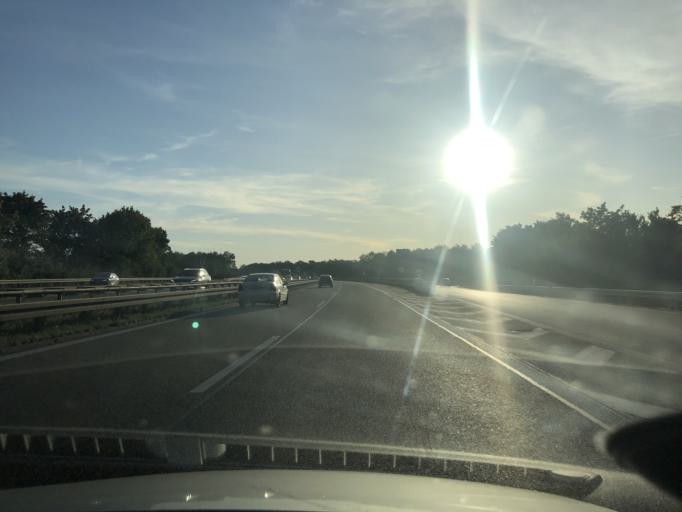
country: DE
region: Baden-Wuerttemberg
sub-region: Regierungsbezirk Stuttgart
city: Boeblingen
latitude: 48.6847
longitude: 8.9745
